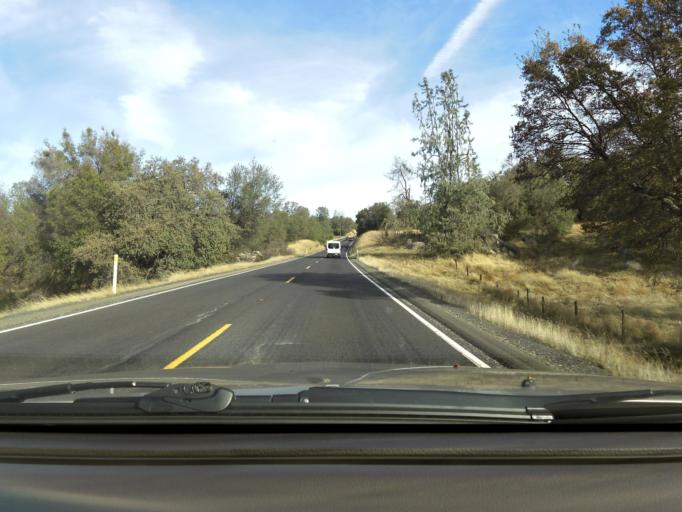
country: US
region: California
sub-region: Madera County
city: Yosemite Lakes
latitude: 37.1788
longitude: -119.7290
